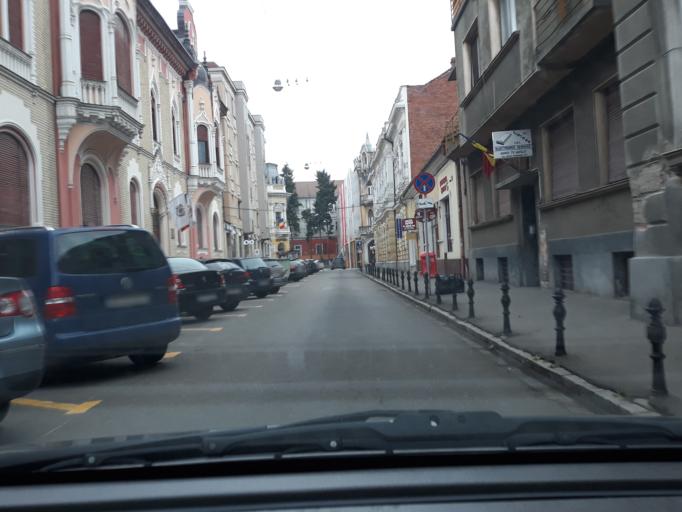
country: RO
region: Bihor
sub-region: Comuna Biharea
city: Oradea
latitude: 47.0590
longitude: 21.9328
